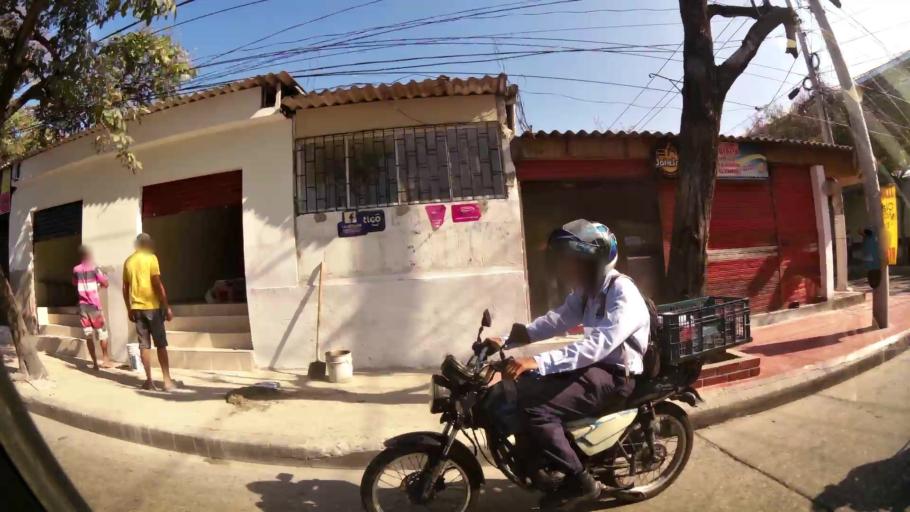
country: CO
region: Atlantico
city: Barranquilla
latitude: 10.9836
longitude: -74.7887
